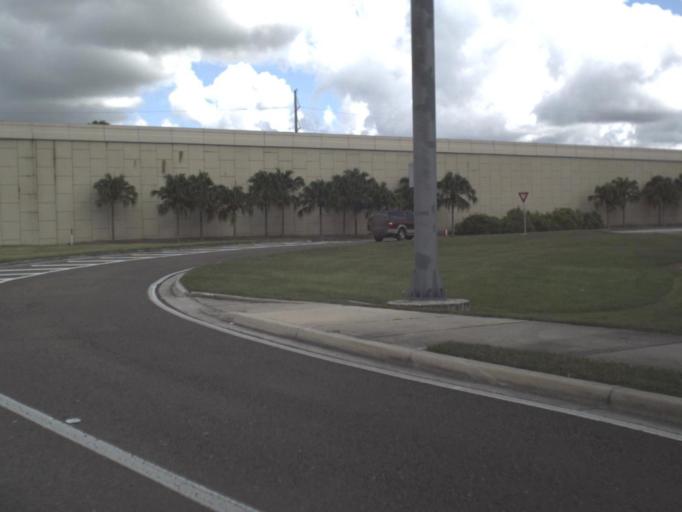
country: US
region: Florida
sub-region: Polk County
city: Gibsonia
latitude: 28.0845
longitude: -81.9693
